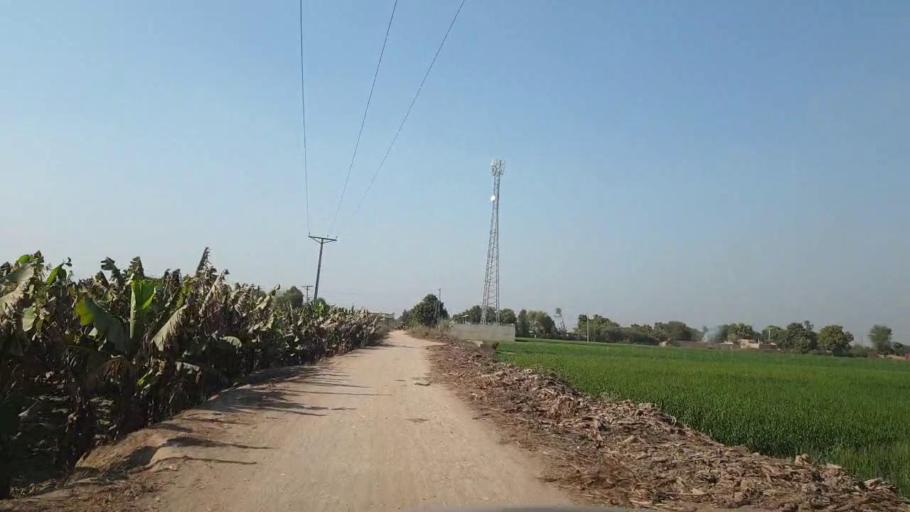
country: PK
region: Sindh
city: Tando Allahyar
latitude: 25.5690
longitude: 68.7095
